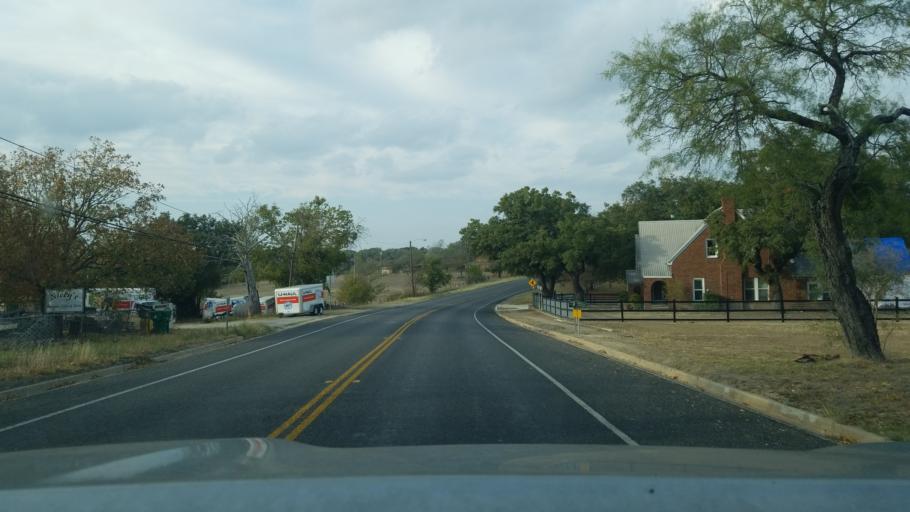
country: US
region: Texas
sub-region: Mills County
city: Goldthwaite
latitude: 31.4616
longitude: -98.5740
